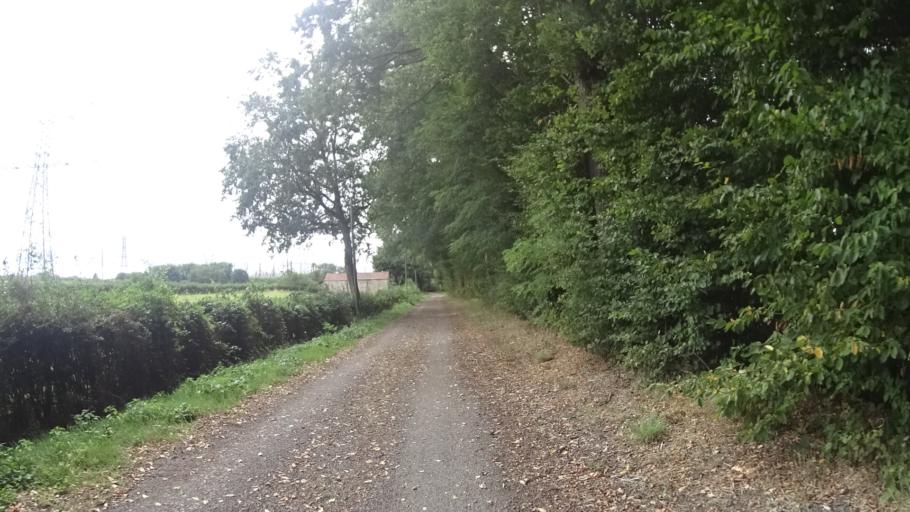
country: FR
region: Bourgogne
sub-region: Departement de Saone-et-Loire
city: Saint-Leu
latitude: 46.7523
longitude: 4.5005
